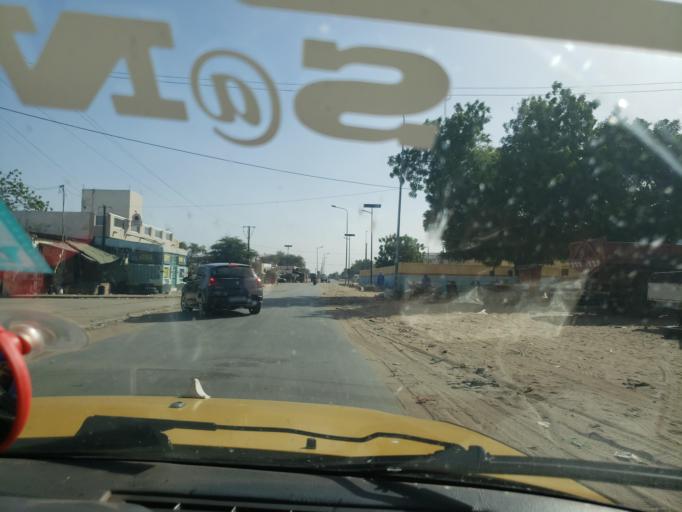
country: SN
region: Louga
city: Louga
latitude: 15.6196
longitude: -16.2107
